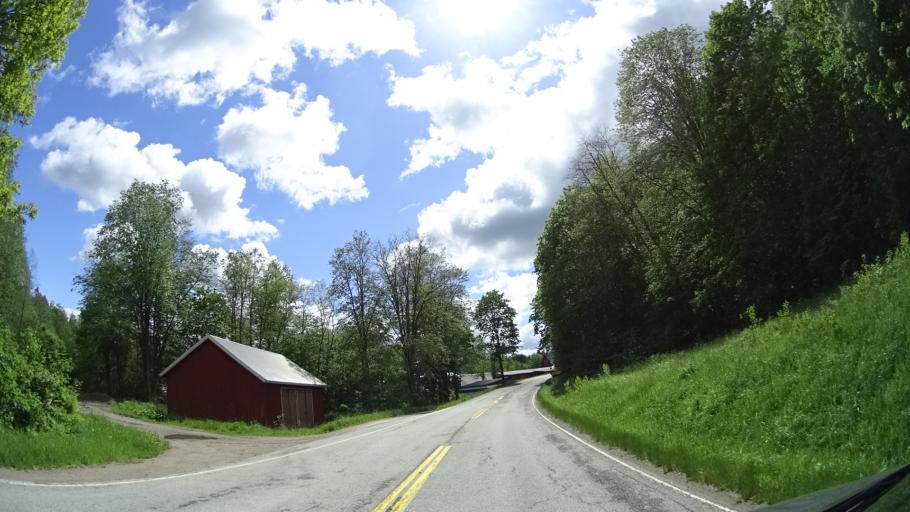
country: FI
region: Uusimaa
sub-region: Raaseporin
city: Pohja
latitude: 60.1344
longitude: 23.5489
